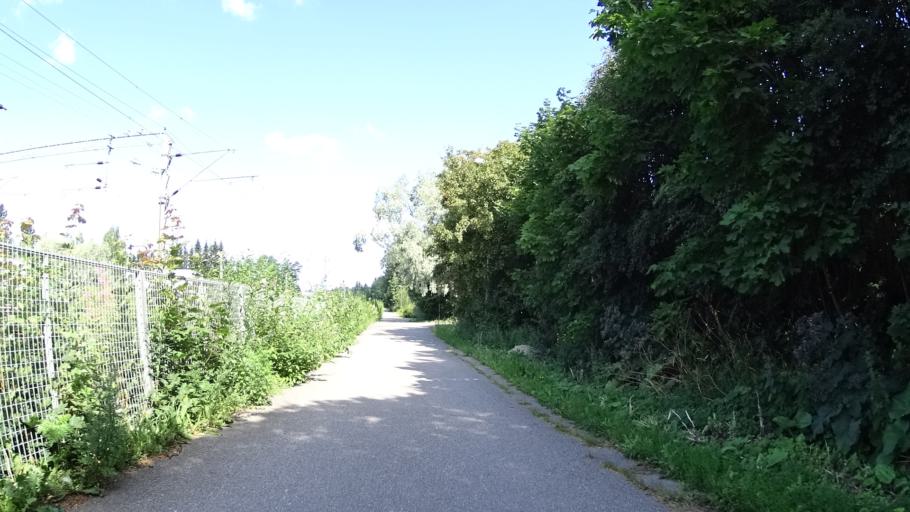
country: FI
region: Uusimaa
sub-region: Helsinki
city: Jaervenpaeae
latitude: 60.4674
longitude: 25.0986
